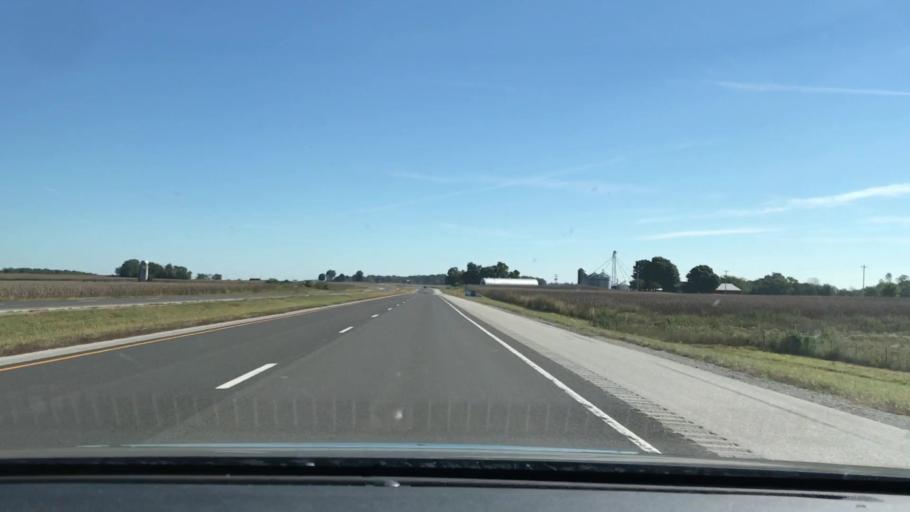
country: US
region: Kentucky
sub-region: Todd County
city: Elkton
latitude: 36.8051
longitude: -87.0605
